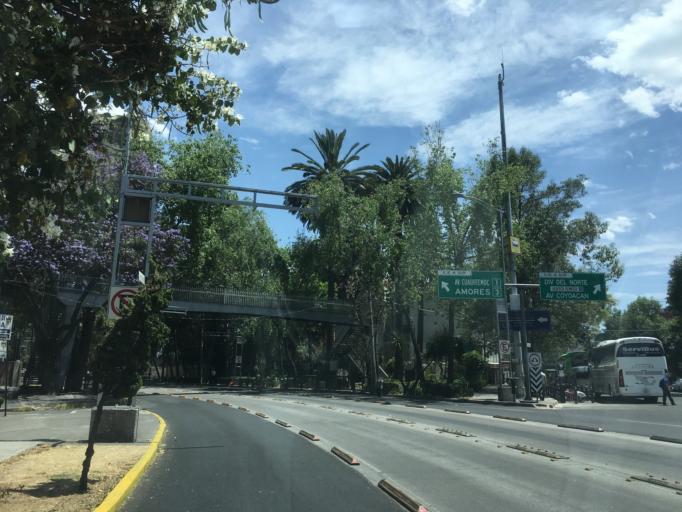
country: MX
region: Mexico City
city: Benito Juarez
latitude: 19.3987
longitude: -99.1673
